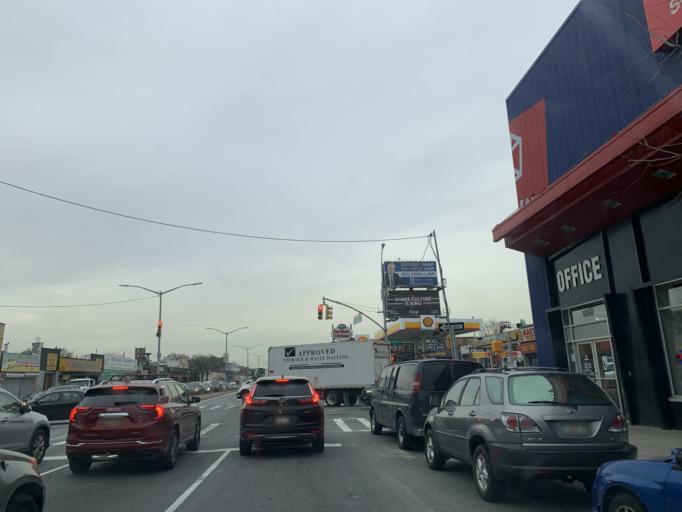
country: US
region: New York
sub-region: Kings County
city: Brooklyn
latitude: 40.6798
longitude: -73.9587
